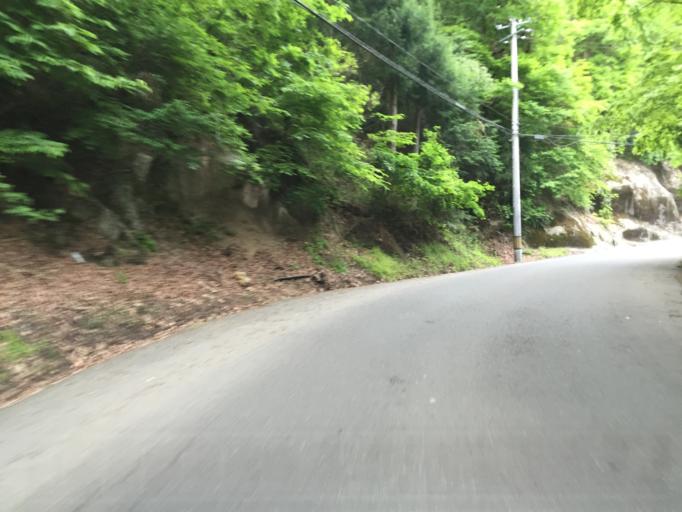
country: JP
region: Fukushima
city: Yanagawamachi-saiwaicho
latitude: 37.8976
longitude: 140.6658
